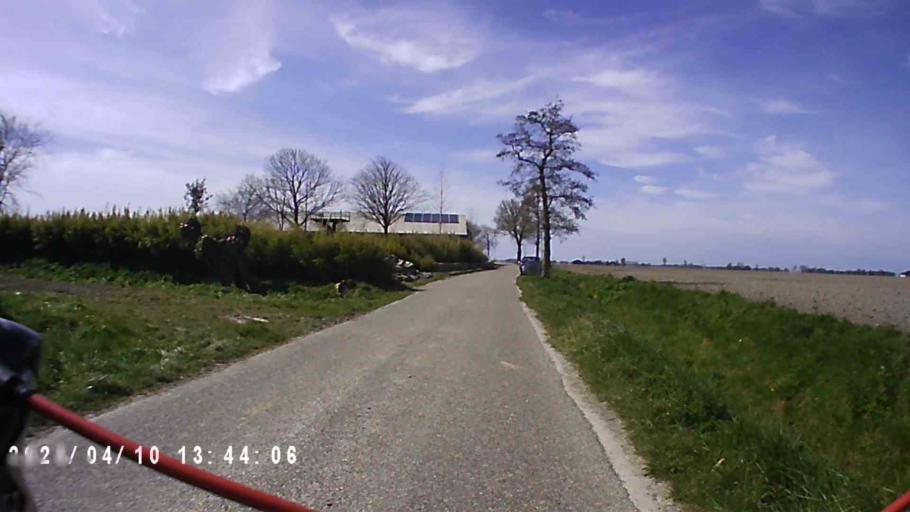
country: NL
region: Groningen
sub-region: Gemeente De Marne
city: Ulrum
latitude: 53.3745
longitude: 6.3796
